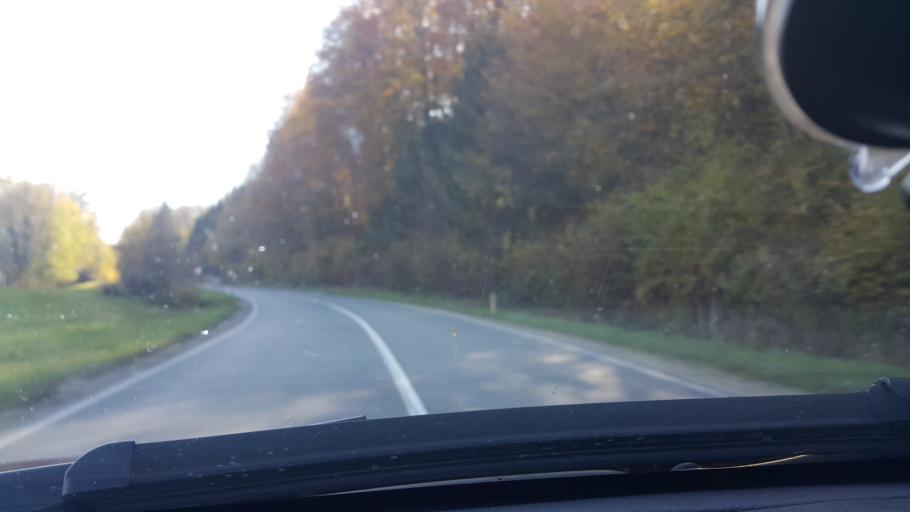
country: SI
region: Podcetrtek
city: Podcetrtek
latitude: 46.1153
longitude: 15.5989
